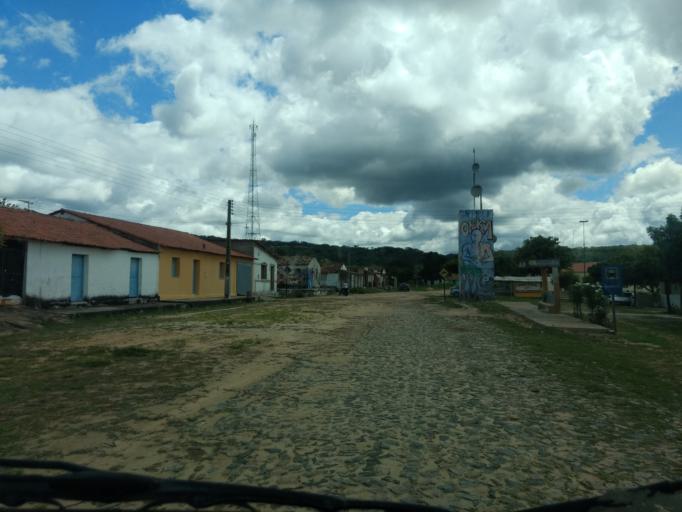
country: BR
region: Ceara
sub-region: Crateus
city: Crateus
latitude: -5.2410
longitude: -40.9179
